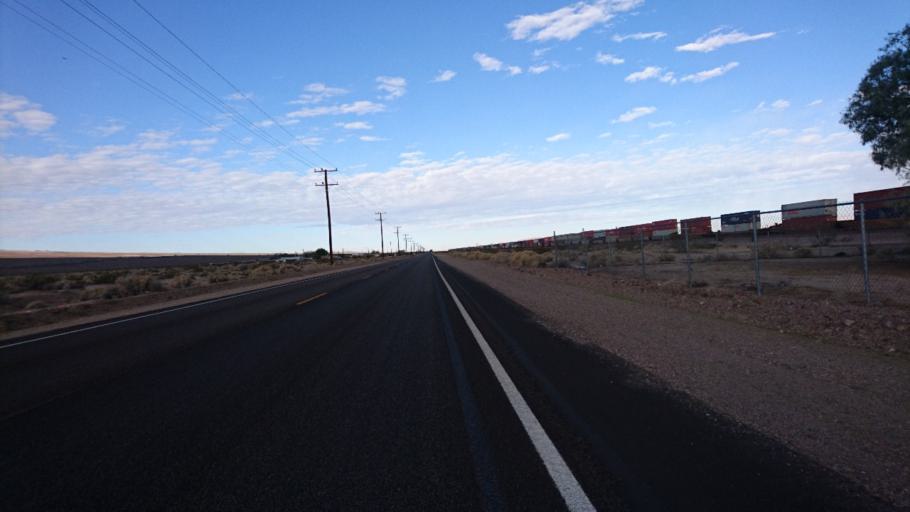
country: US
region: California
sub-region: San Bernardino County
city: Barstow
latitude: 34.8448
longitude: -116.7719
